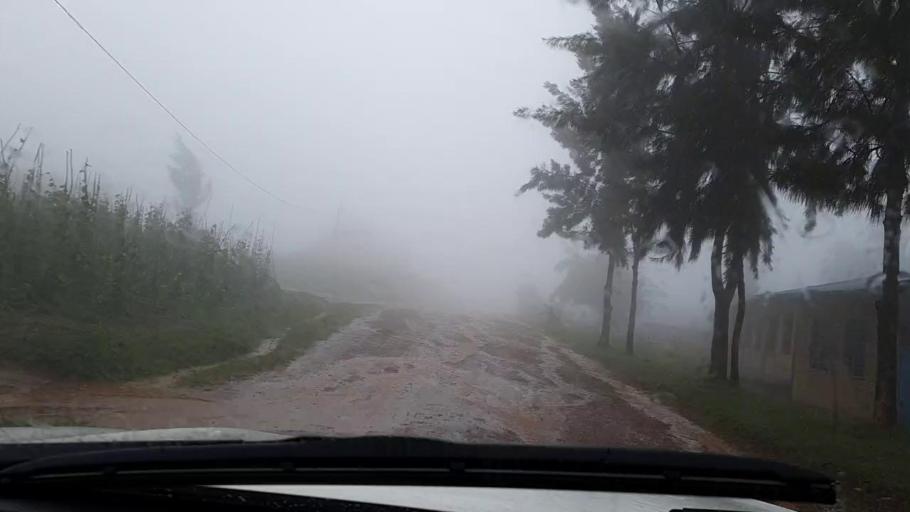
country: RW
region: Northern Province
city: Byumba
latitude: -1.7328
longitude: 30.0241
